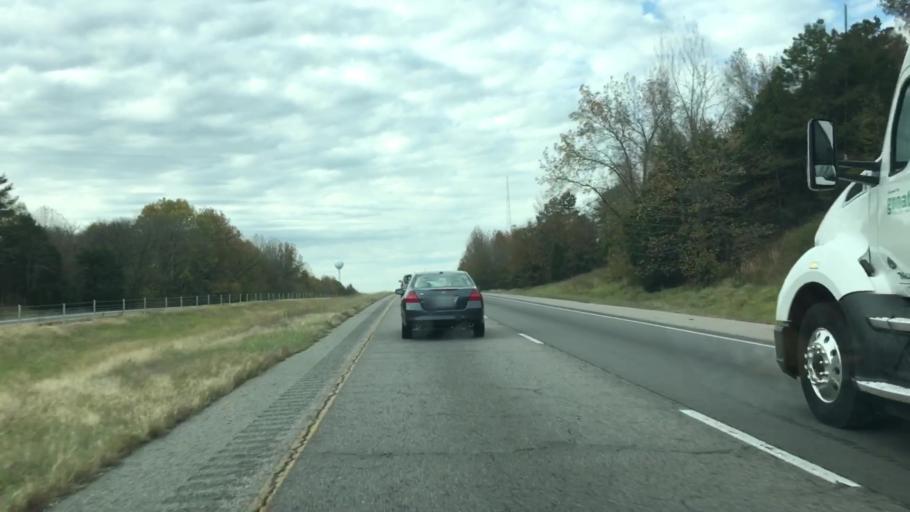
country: US
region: Arkansas
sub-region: Faulkner County
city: Conway
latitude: 35.1445
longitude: -92.5339
